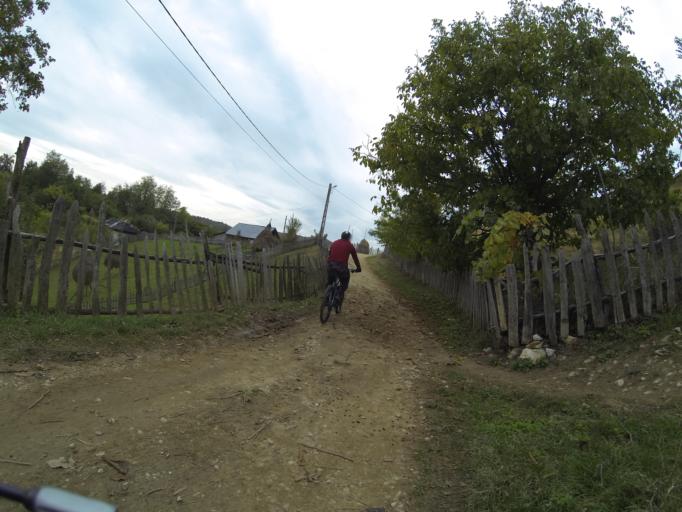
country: RO
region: Gorj
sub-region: Comuna Tismana
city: Sohodol
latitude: 45.0595
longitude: 22.8833
